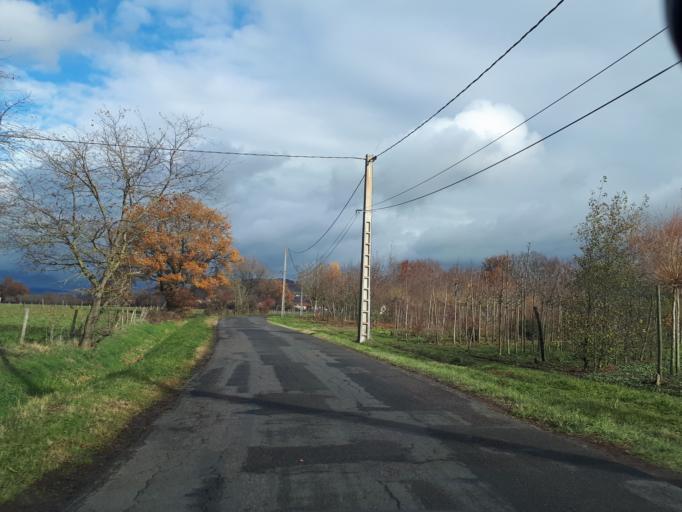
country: FR
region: Rhone-Alpes
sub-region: Departement de la Loire
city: Saint-Andre-le-Puy
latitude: 45.6300
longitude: 4.2768
